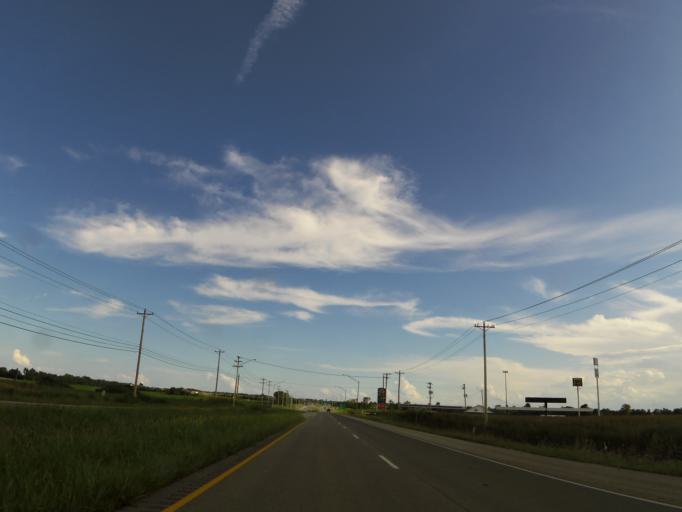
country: US
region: Kentucky
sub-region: Christian County
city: Oak Grove
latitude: 36.7115
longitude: -87.4577
